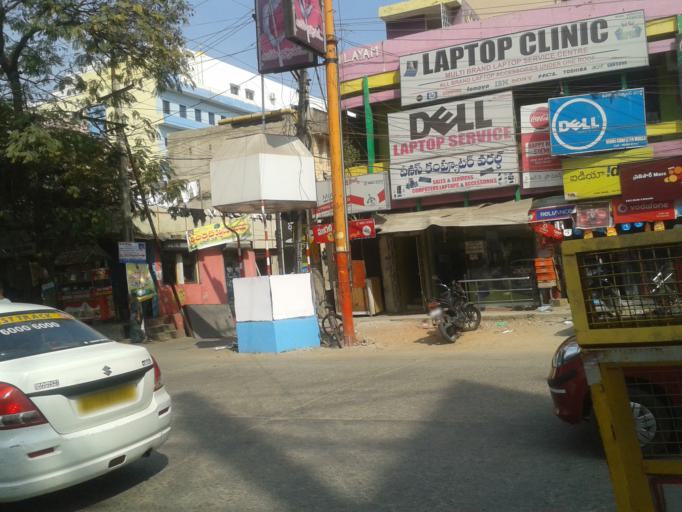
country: IN
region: Andhra Pradesh
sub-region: Chittoor
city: Tirupati
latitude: 13.6391
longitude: 79.4186
